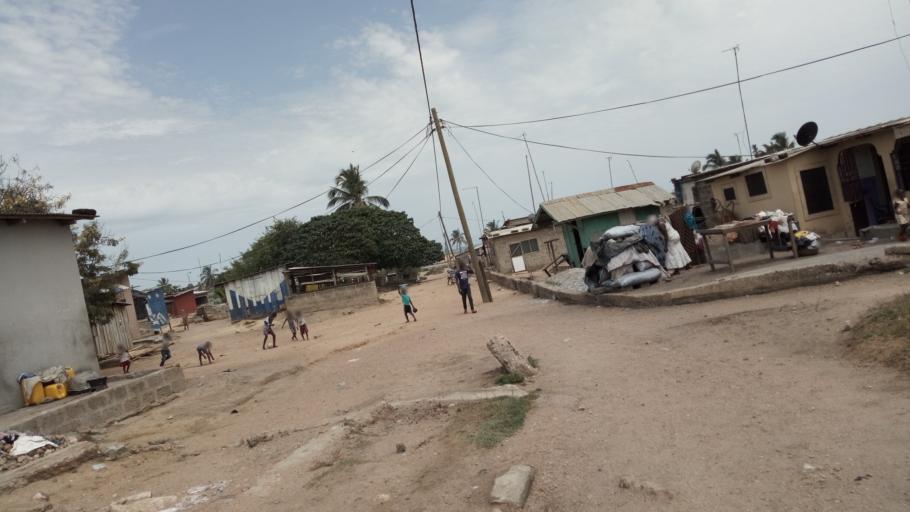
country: GH
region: Central
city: Winneba
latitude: 5.3496
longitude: -0.6159
